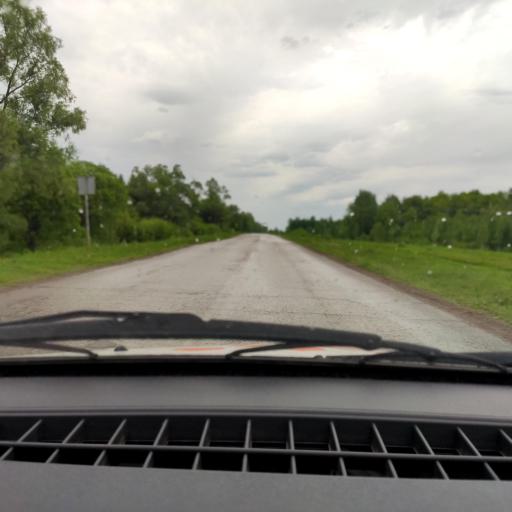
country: RU
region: Bashkortostan
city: Urman
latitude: 54.8591
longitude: 56.8349
